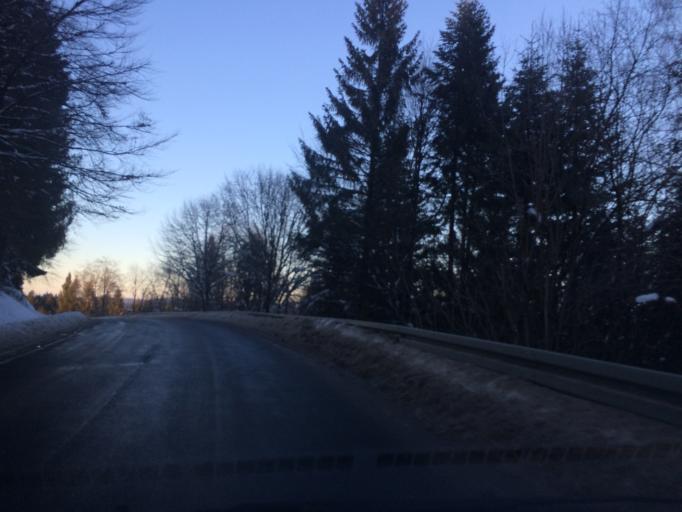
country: PL
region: Subcarpathian Voivodeship
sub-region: Powiat bieszczadzki
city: Lutowiska
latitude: 49.2741
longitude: 22.6862
